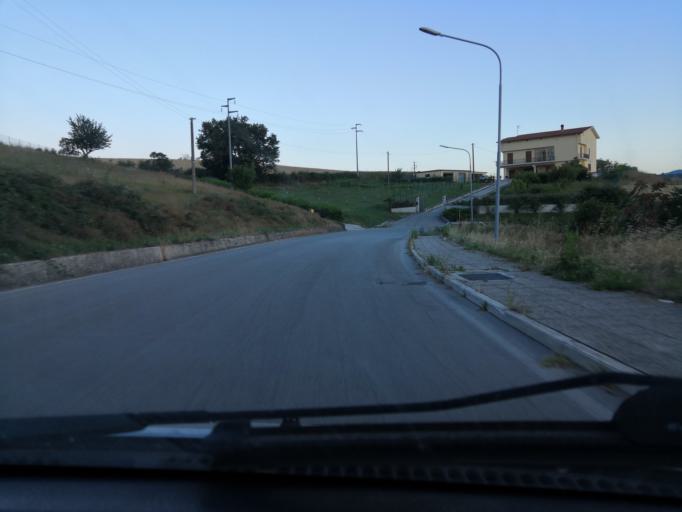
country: IT
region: Molise
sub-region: Provincia di Campobasso
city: Jelsi
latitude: 41.5155
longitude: 14.7944
